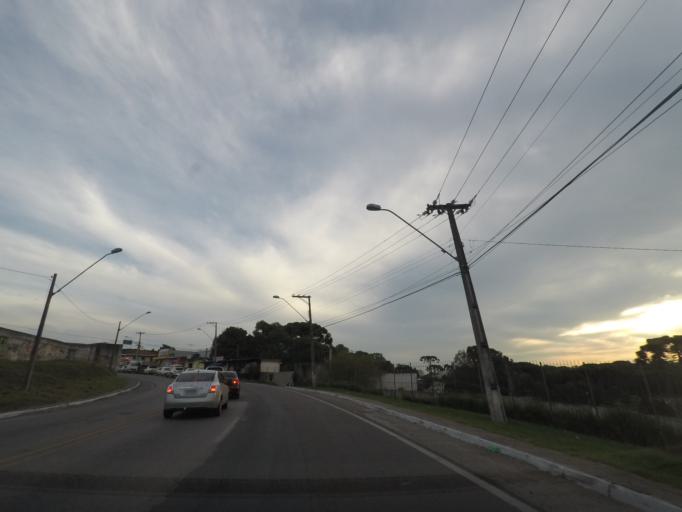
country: BR
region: Parana
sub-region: Curitiba
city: Curitiba
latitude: -25.3734
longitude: -49.2227
